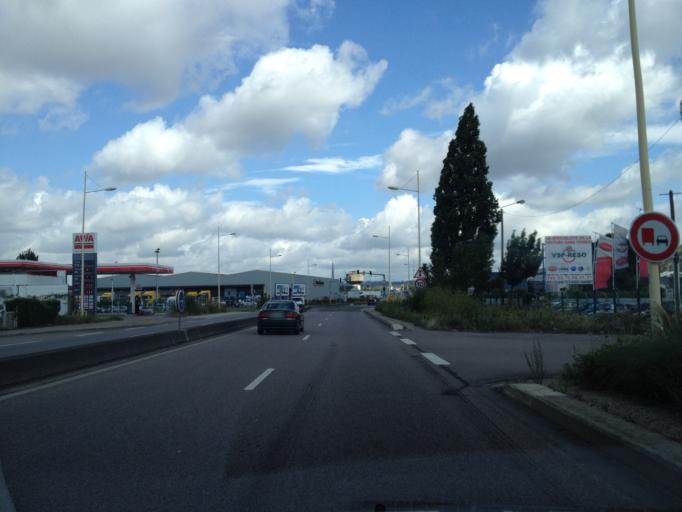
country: FR
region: Haute-Normandie
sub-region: Departement de la Seine-Maritime
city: Sotteville-les-Rouen
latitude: 49.4201
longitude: 1.1073
